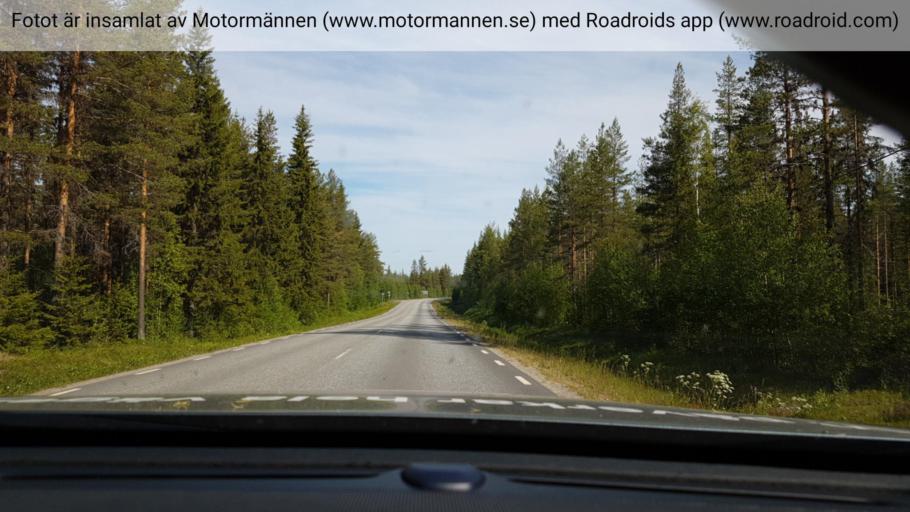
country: SE
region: Vaesterbotten
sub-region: Dorotea Kommun
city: Dorotea
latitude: 64.2798
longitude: 16.3444
